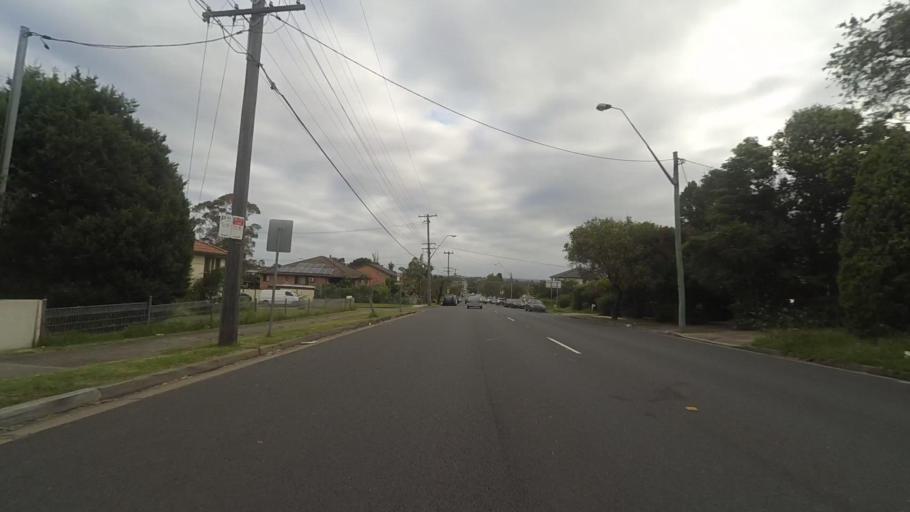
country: AU
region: New South Wales
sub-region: Bankstown
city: Revesby
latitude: -33.9272
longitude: 151.0122
